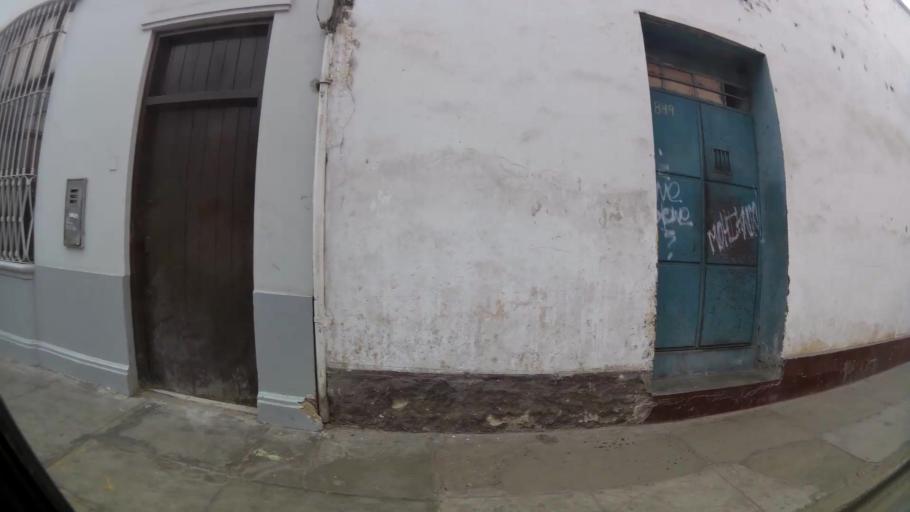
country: PE
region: La Libertad
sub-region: Provincia de Trujillo
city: Trujillo
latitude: -8.1071
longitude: -79.0255
